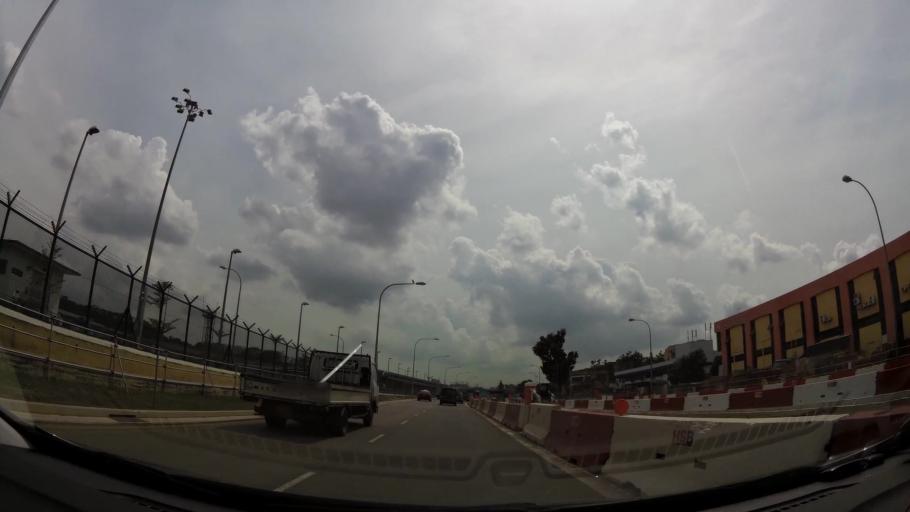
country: MY
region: Johor
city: Johor Bahru
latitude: 1.4003
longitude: 103.7559
